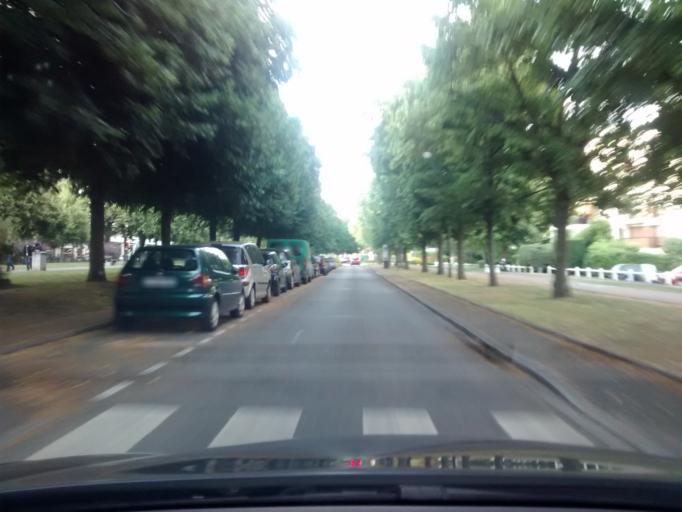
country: FR
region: Ile-de-France
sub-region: Departement des Yvelines
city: Le Chesnay
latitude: 48.8252
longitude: 2.1189
